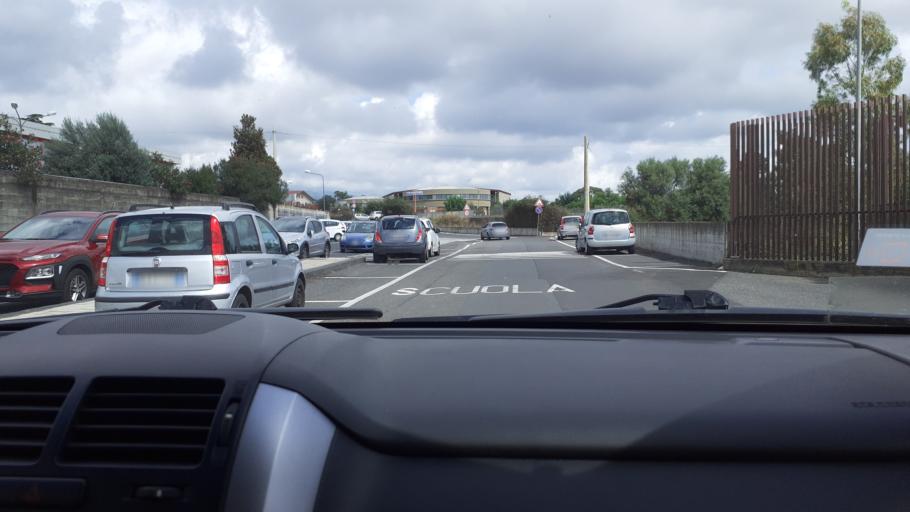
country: IT
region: Sicily
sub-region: Catania
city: San Giovanni la Punta
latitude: 37.5787
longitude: 15.1013
